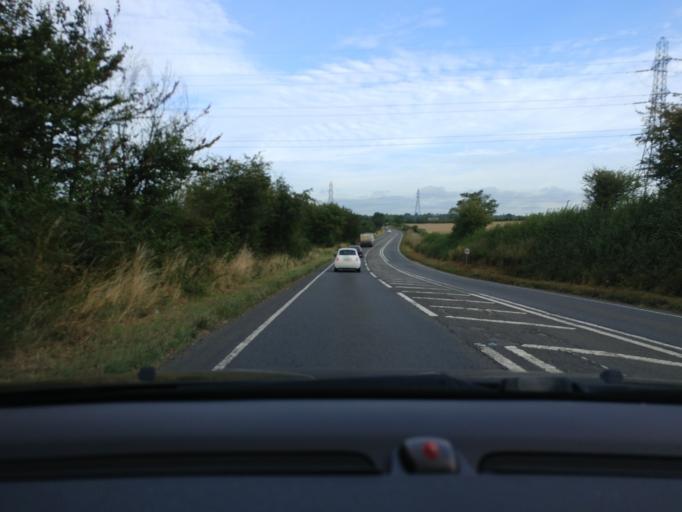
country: GB
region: England
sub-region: Oxfordshire
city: Radley
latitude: 51.6996
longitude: -1.2130
